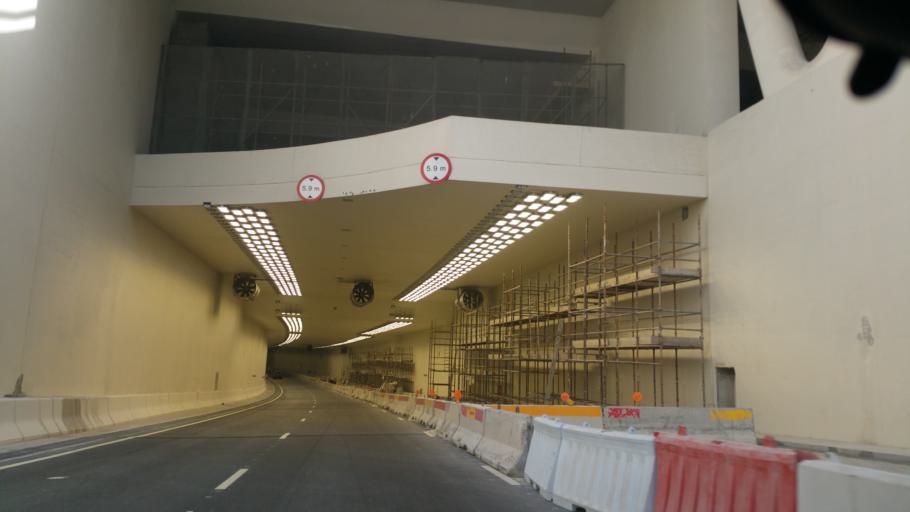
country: QA
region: Baladiyat Umm Salal
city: Umm Salal Muhammad
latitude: 25.4201
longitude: 51.5059
